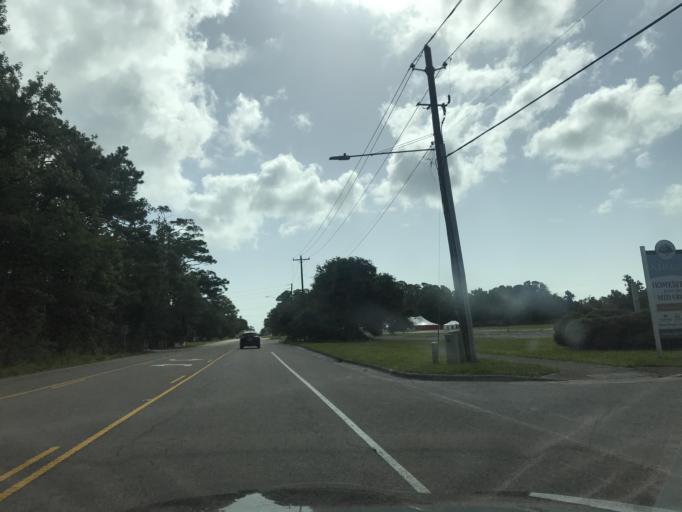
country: US
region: North Carolina
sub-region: New Hanover County
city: Seagate
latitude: 34.2205
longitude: -77.8273
